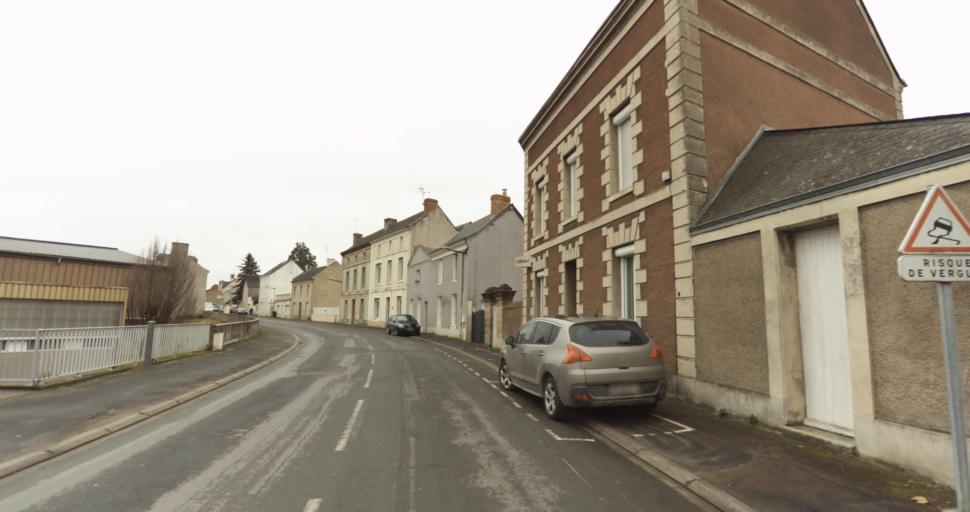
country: FR
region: Pays de la Loire
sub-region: Departement de Maine-et-Loire
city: Doue-la-Fontaine
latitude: 47.1908
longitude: -0.2747
